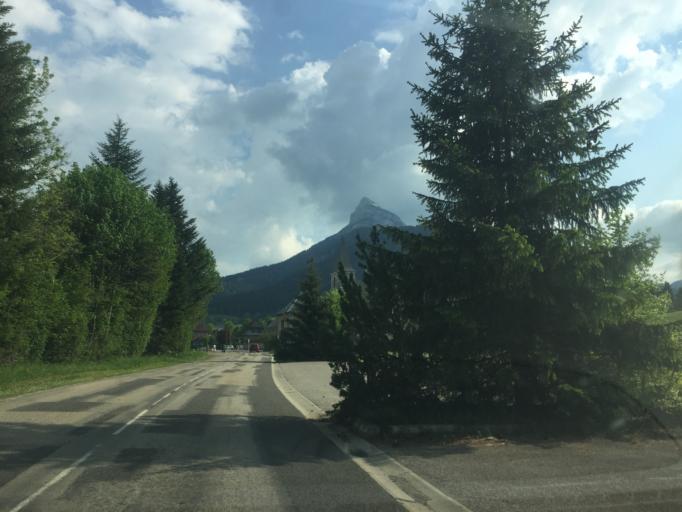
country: FR
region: Rhone-Alpes
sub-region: Departement de l'Isere
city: Le Sappey-en-Chartreuse
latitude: 45.3248
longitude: 5.8067
